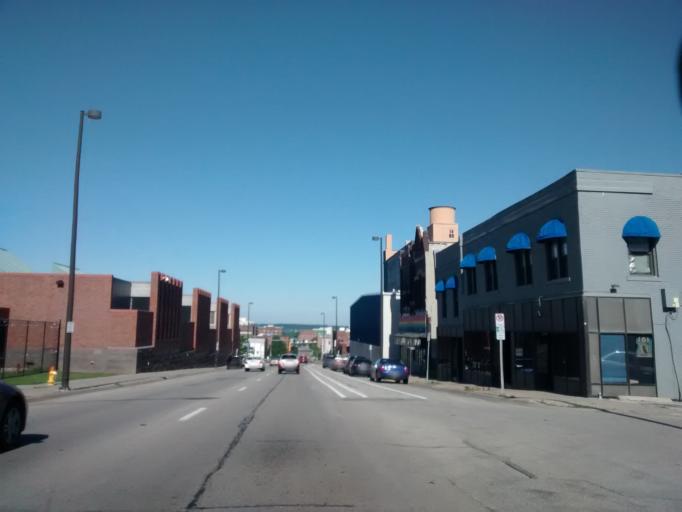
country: US
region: Nebraska
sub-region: Douglas County
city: Omaha
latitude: 41.2524
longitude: -95.9397
